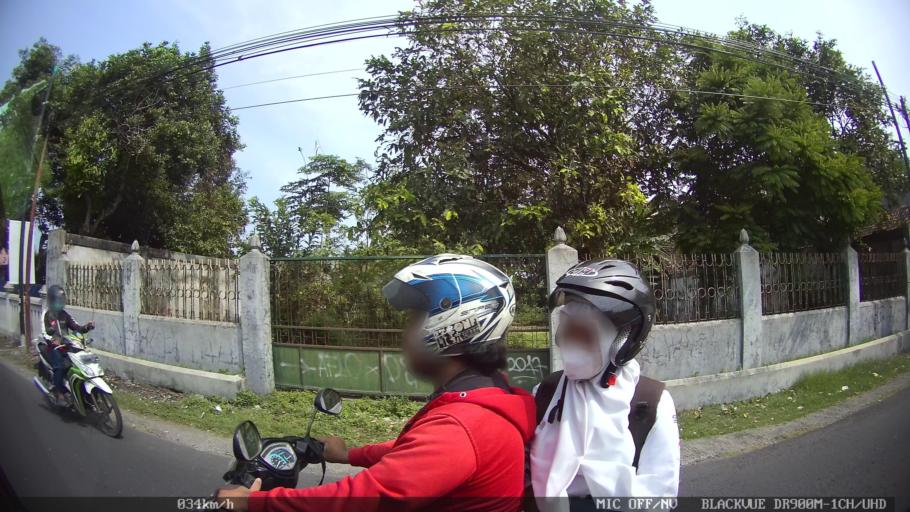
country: ID
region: Daerah Istimewa Yogyakarta
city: Depok
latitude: -7.8035
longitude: 110.4299
